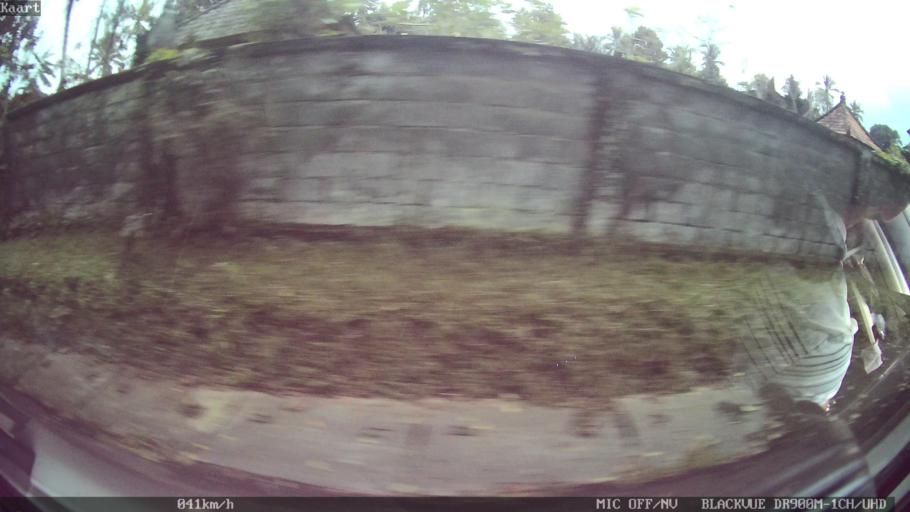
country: ID
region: Bali
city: Pemijian
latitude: -8.4502
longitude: 115.2286
